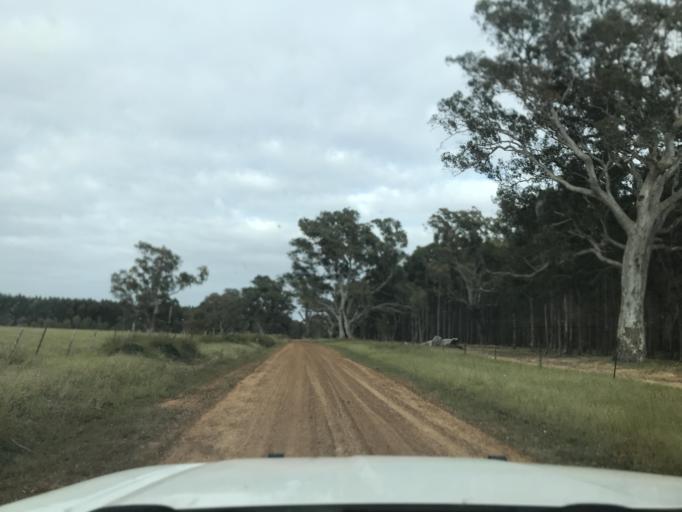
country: AU
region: South Australia
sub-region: Wattle Range
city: Penola
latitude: -37.2795
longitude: 141.3921
